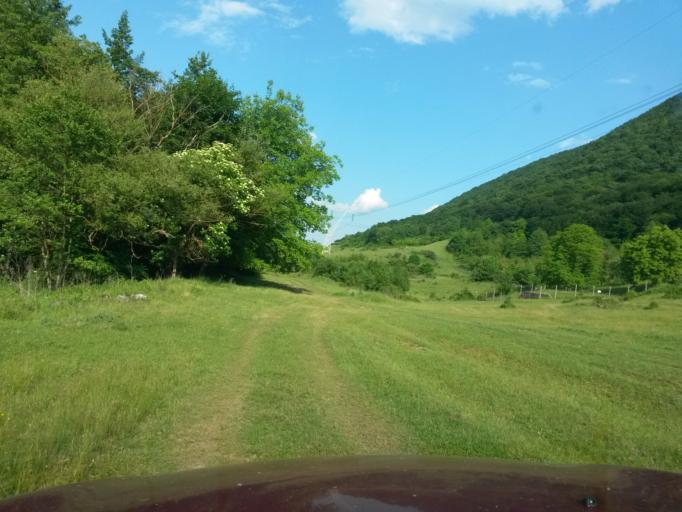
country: SK
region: Kosicky
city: Roznava
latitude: 48.5839
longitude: 20.6855
